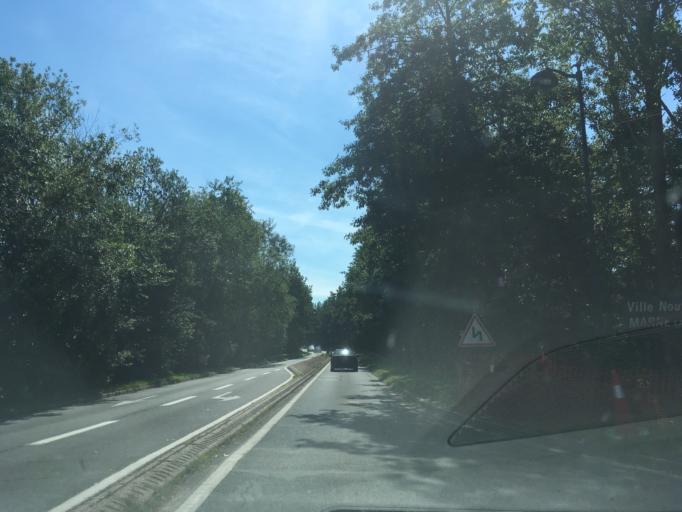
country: FR
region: Ile-de-France
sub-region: Departement de Seine-et-Marne
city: Bailly-Romainvilliers
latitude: 48.8498
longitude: 2.8296
